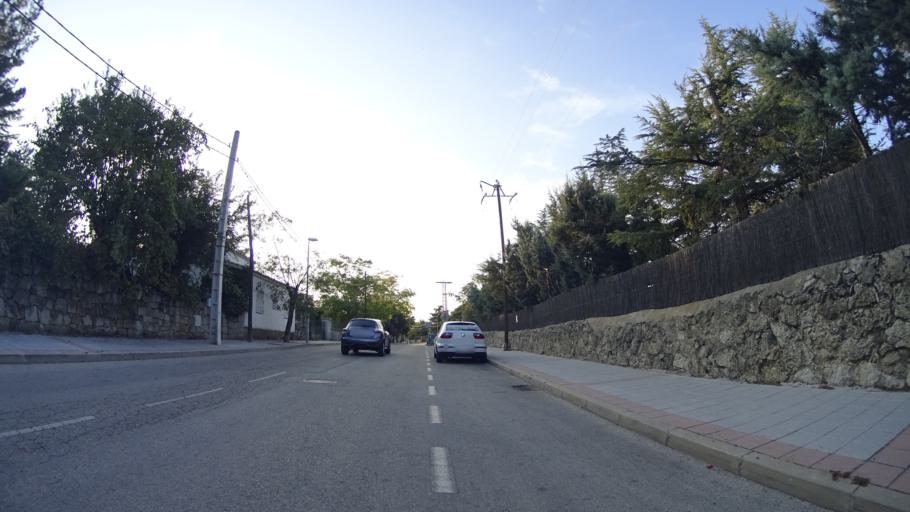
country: ES
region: Madrid
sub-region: Provincia de Madrid
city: Galapagar
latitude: 40.5761
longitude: -3.9928
